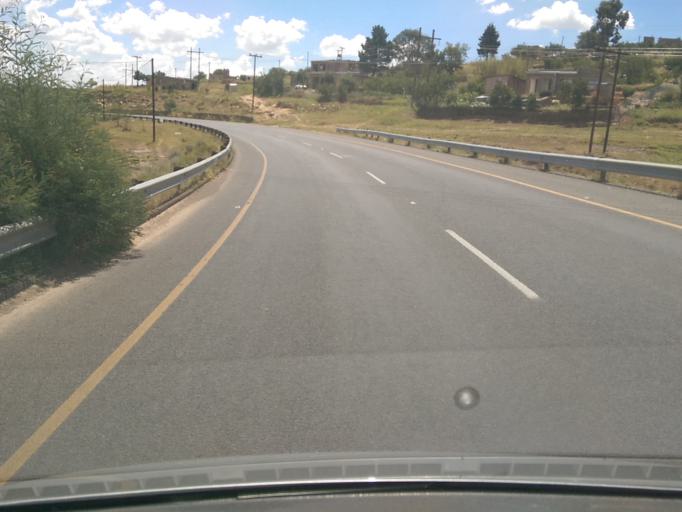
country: LS
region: Maseru
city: Maseru
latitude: -29.3771
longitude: 27.4950
